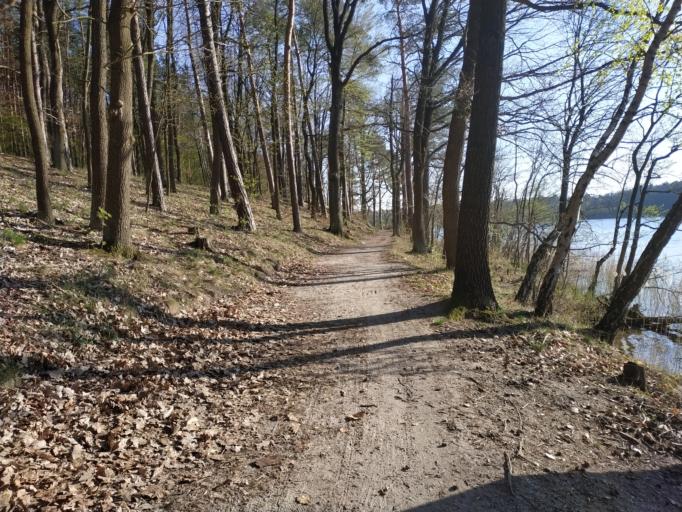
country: DE
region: Brandenburg
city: Strausberg
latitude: 52.5712
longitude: 13.8320
